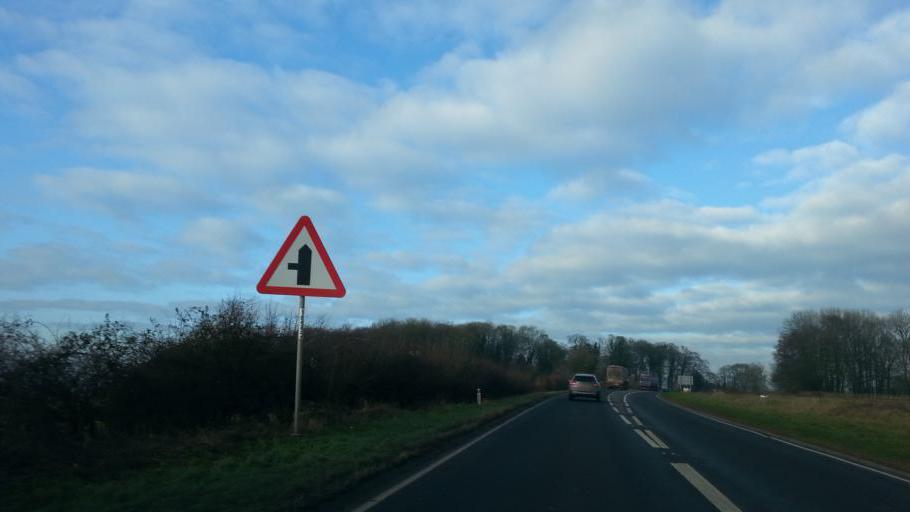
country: GB
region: England
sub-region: South Gloucestershire
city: Cold Ashton
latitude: 51.4673
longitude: -2.3655
